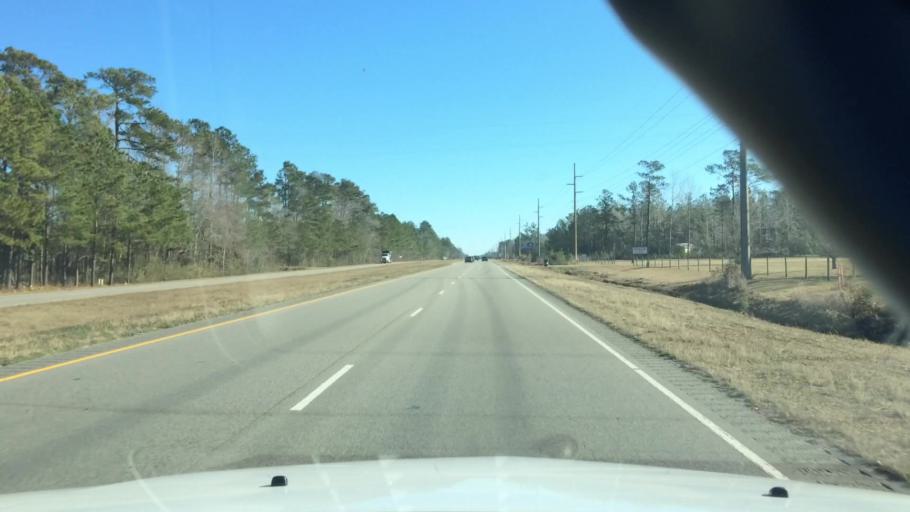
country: US
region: North Carolina
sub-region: Brunswick County
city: Shallotte
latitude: 33.9997
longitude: -78.3206
